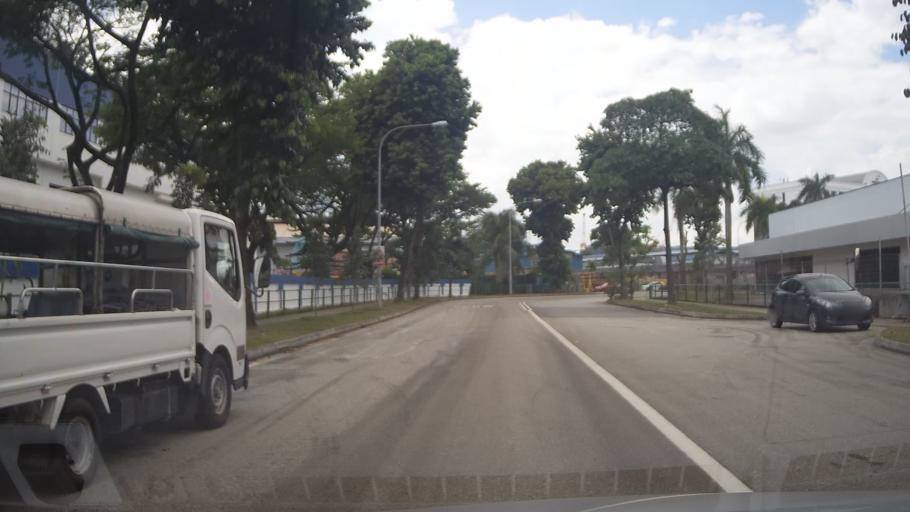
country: SG
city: Singapore
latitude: 1.3020
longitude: 103.7608
